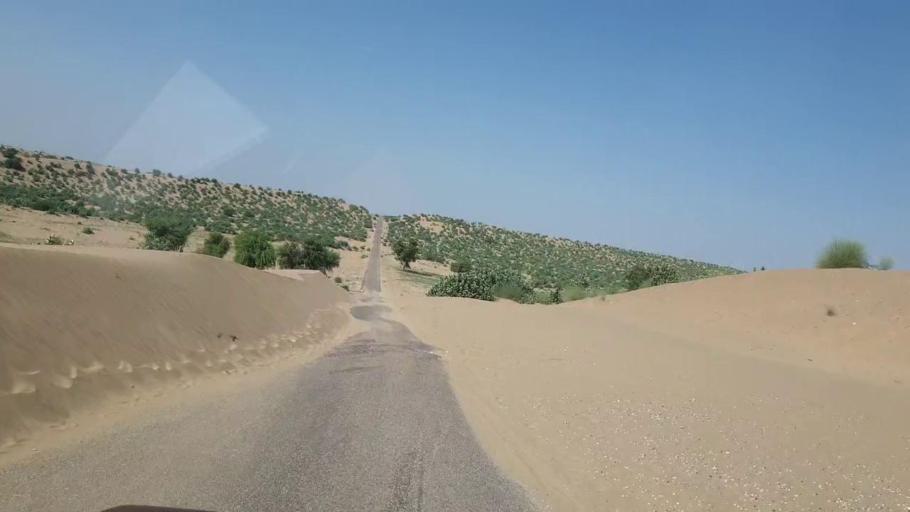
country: PK
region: Sindh
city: Chor
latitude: 25.6155
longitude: 70.3178
